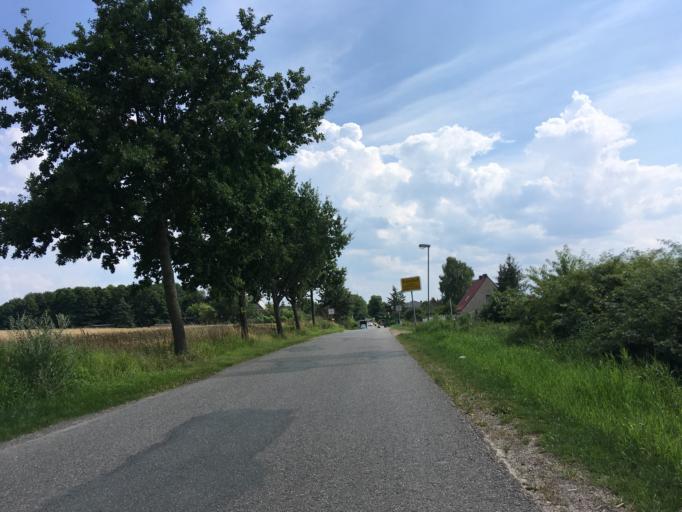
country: DE
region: Brandenburg
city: Glienicke
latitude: 52.6618
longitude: 13.3352
